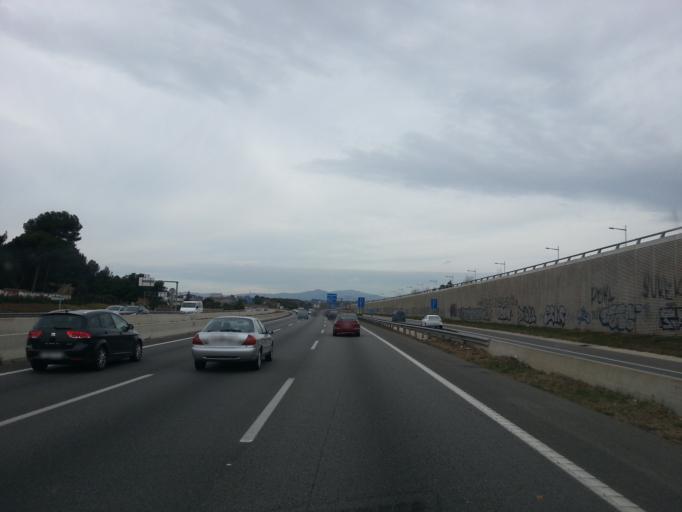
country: ES
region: Catalonia
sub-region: Provincia de Barcelona
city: Sant Quirze del Valles
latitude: 41.5382
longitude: 2.0863
